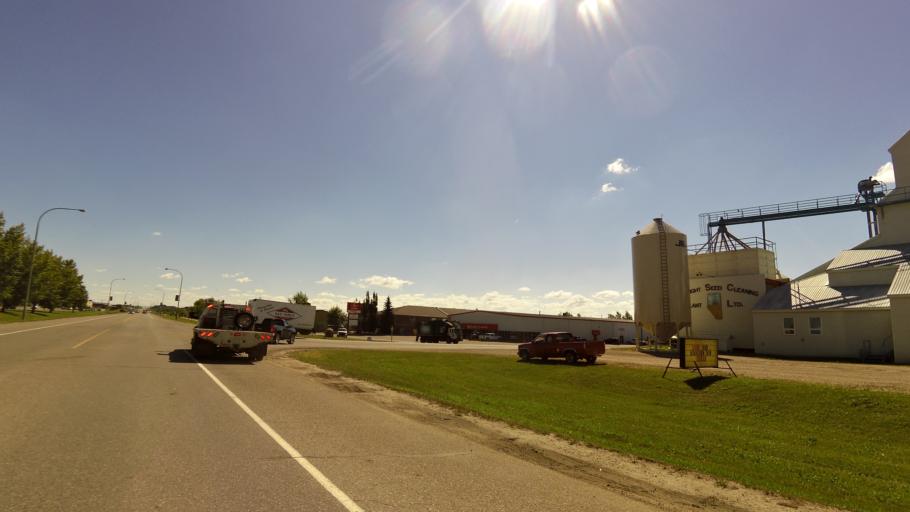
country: CA
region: Alberta
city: Wainwright
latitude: 52.8434
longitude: -110.8457
